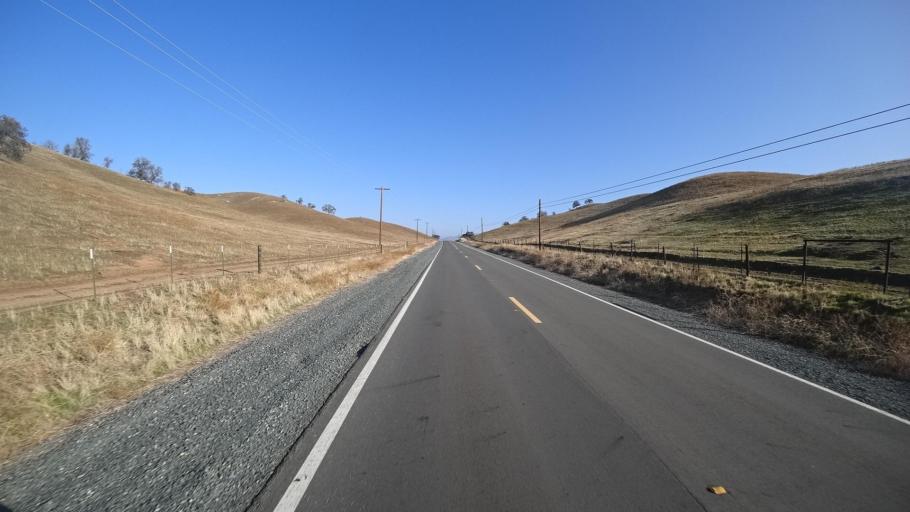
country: US
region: California
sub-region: Tulare County
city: Richgrove
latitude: 35.7217
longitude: -118.8587
